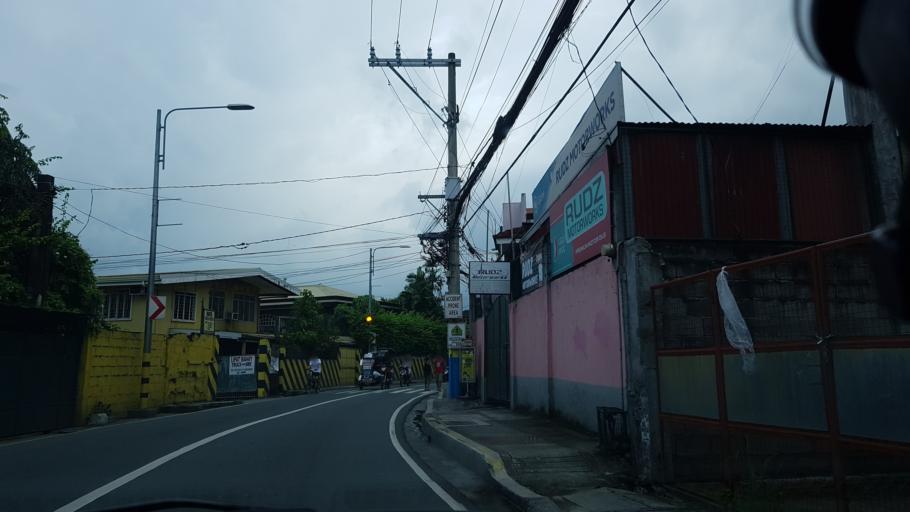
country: PH
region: Calabarzon
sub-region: Province of Rizal
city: Pateros
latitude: 14.5486
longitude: 121.0725
